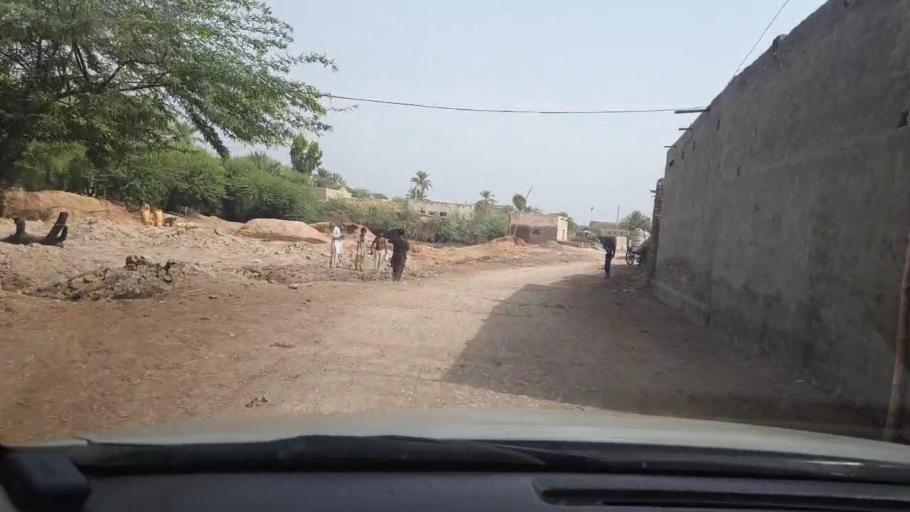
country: PK
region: Sindh
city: Shikarpur
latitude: 28.0044
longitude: 68.5929
